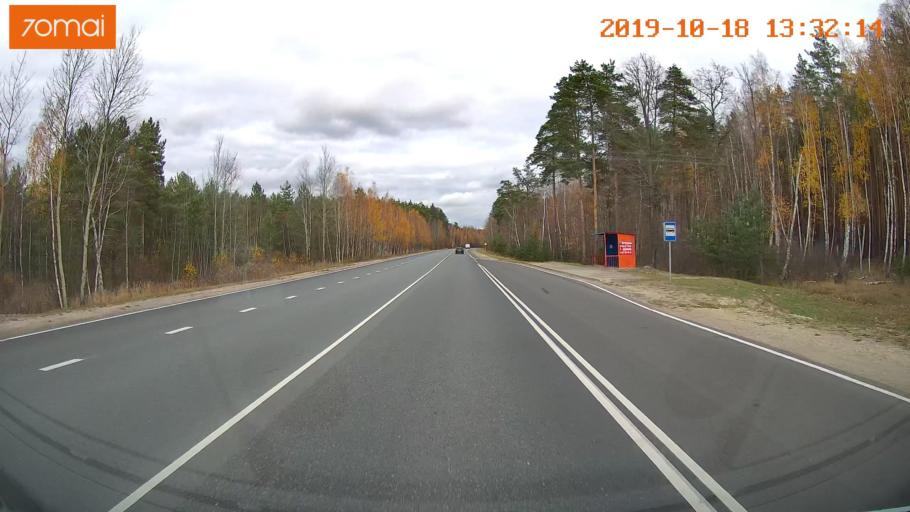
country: RU
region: Rjazan
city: Solotcha
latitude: 54.8304
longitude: 39.9158
